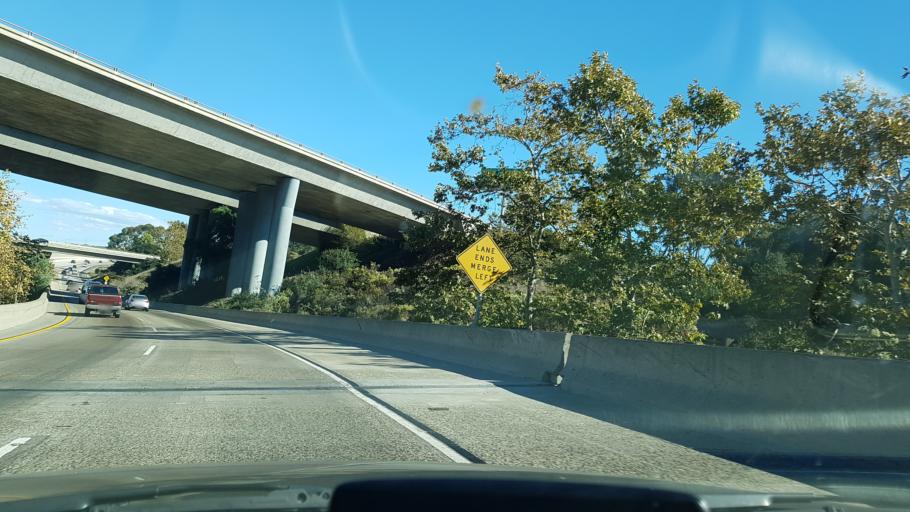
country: US
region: California
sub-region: San Diego County
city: La Jolla
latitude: 32.8470
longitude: -117.1788
